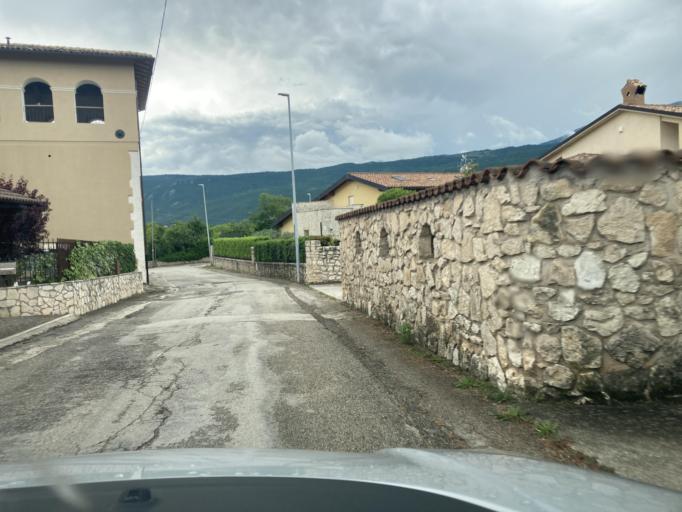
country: IT
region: Abruzzo
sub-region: Provincia dell' Aquila
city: San Demetrio Ne' Vestini
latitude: 42.2914
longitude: 13.5580
